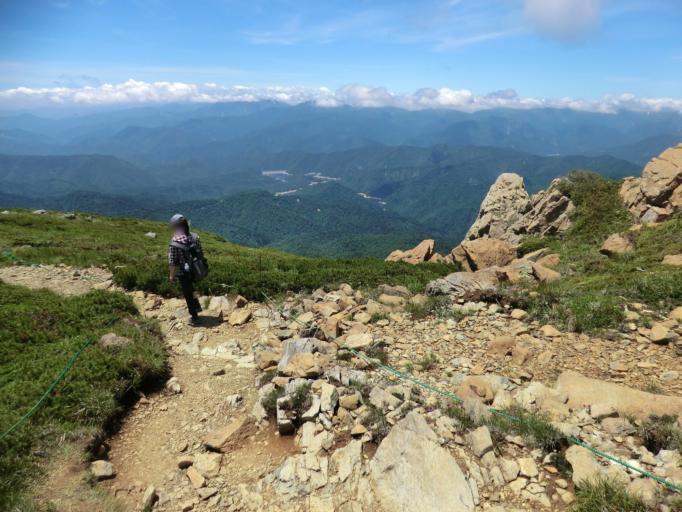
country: JP
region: Gunma
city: Numata
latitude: 36.9010
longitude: 139.1717
